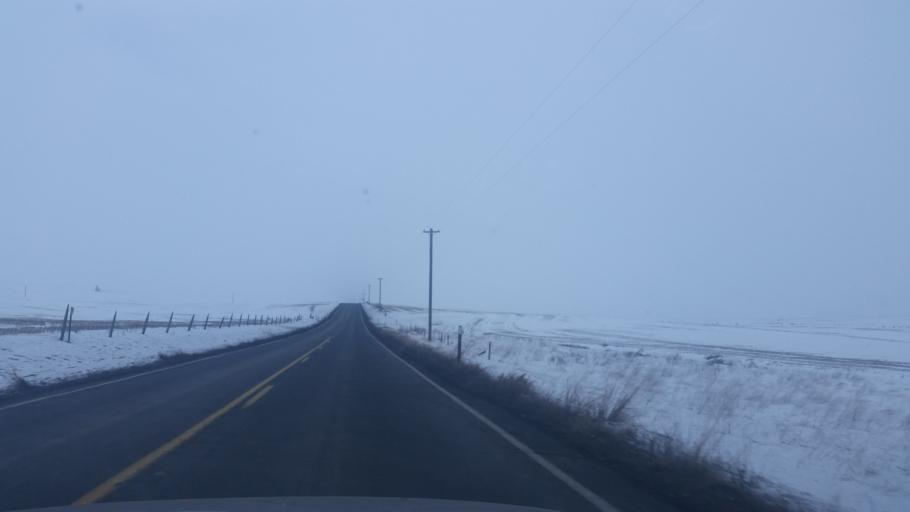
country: US
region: Washington
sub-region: Spokane County
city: Medical Lake
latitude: 47.7064
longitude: -117.8759
